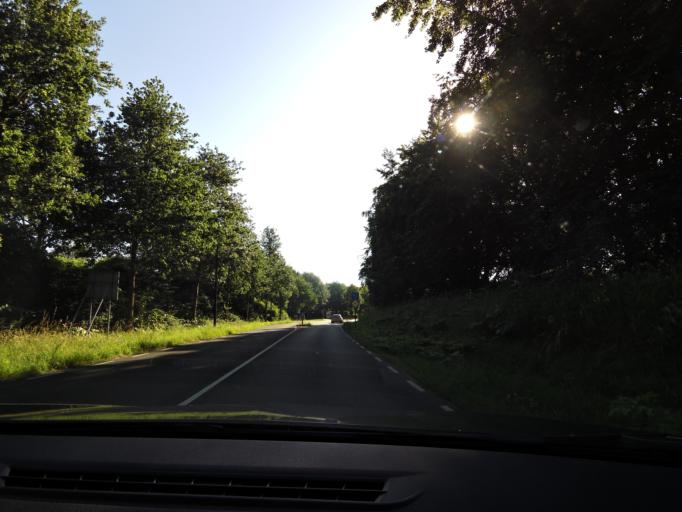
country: NL
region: Overijssel
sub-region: Gemeente Deventer
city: Schalkhaar
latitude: 52.2603
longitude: 6.1798
